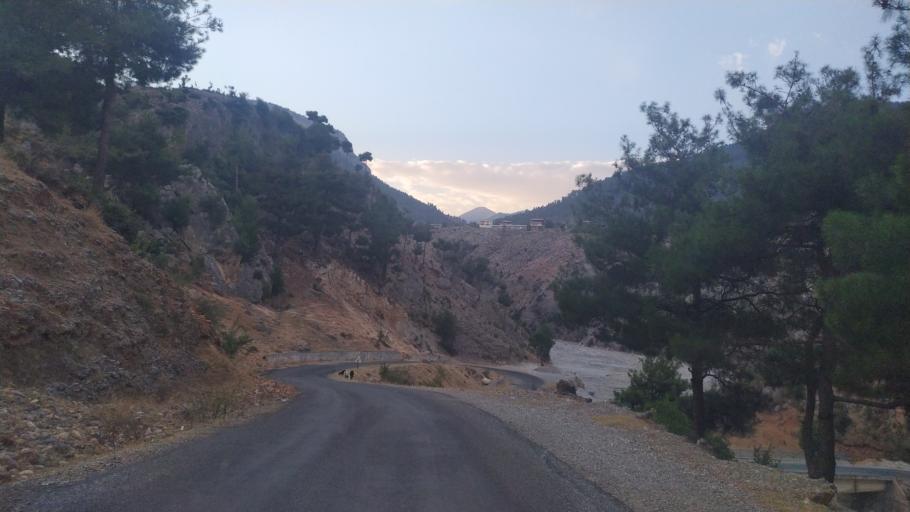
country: TR
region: Mersin
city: Camliyayla
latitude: 37.2390
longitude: 34.7136
